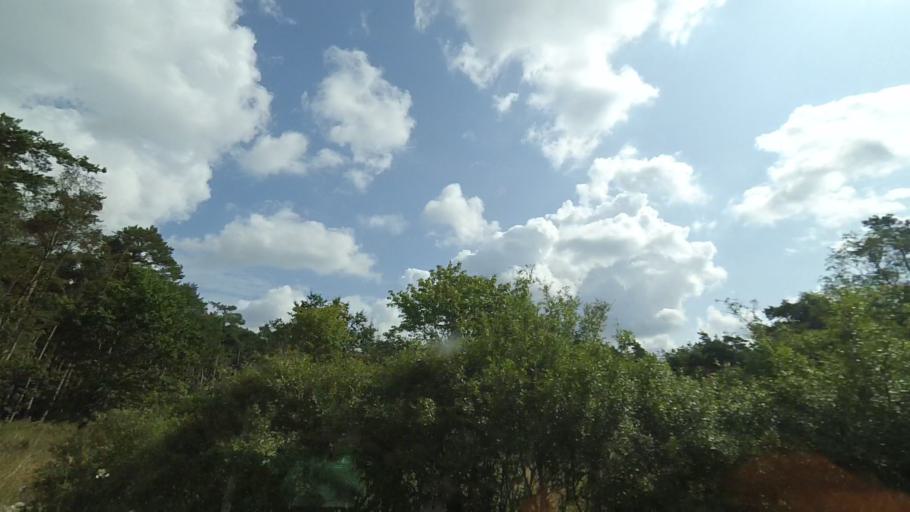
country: DK
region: Central Jutland
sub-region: Norddjurs Kommune
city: Allingabro
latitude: 56.5122
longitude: 10.3948
